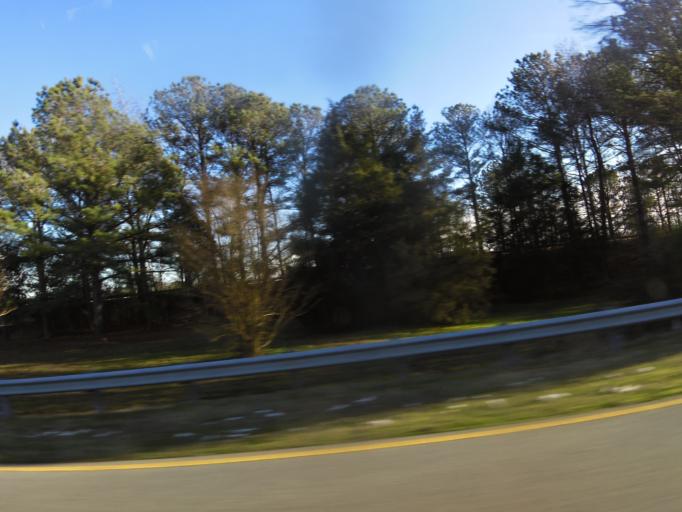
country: US
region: Virginia
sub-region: Isle of Wight County
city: Windsor
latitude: 36.6850
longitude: -76.7696
